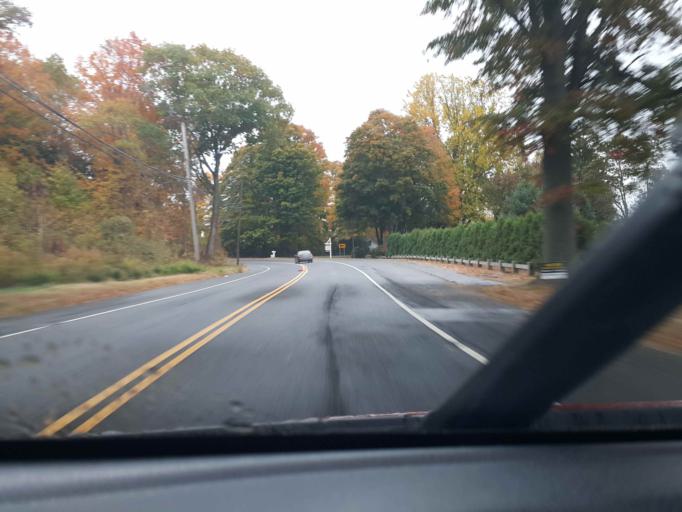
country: US
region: Connecticut
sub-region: New Haven County
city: Madison Center
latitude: 41.2771
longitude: -72.6125
